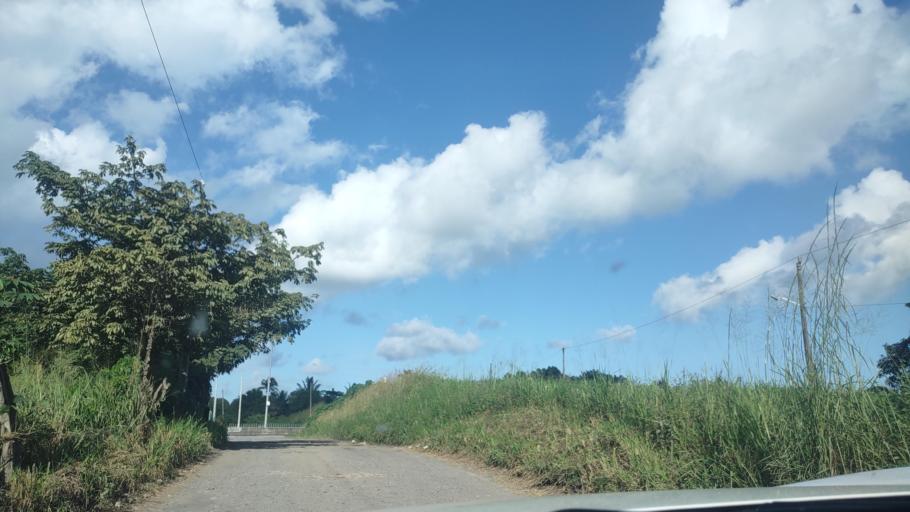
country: MX
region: Veracruz
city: El Tejar
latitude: 19.0636
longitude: -96.1771
